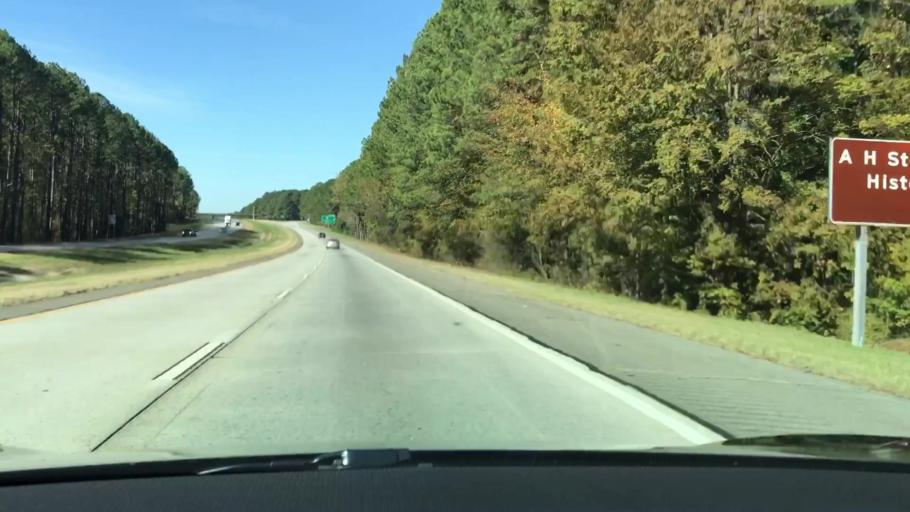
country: US
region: Georgia
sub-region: Taliaferro County
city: Crawfordville
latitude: 33.5291
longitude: -82.8998
